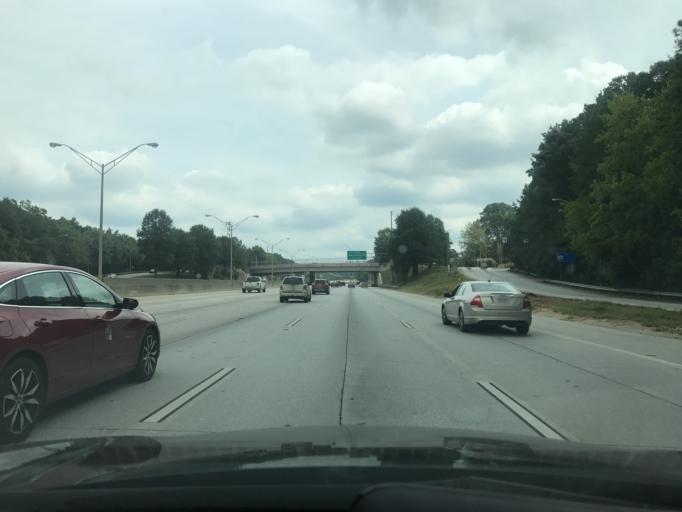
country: US
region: Georgia
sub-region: DeKalb County
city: Druid Hills
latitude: 33.7415
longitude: -84.3306
